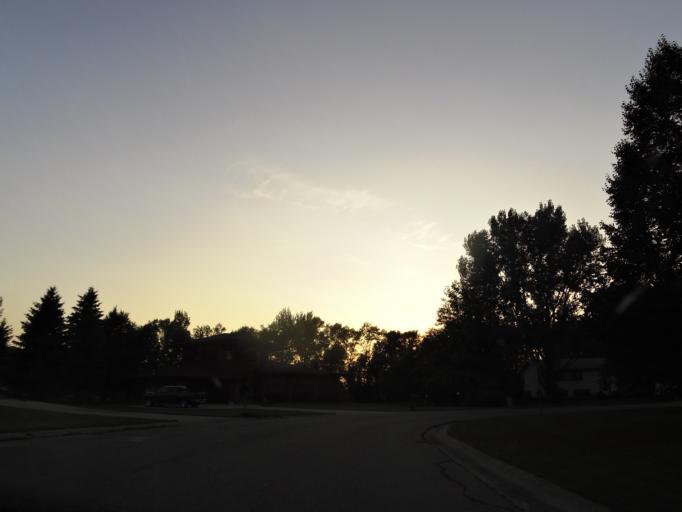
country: US
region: North Dakota
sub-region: Grand Forks County
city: Grand Forks
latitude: 47.8536
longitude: -97.0110
